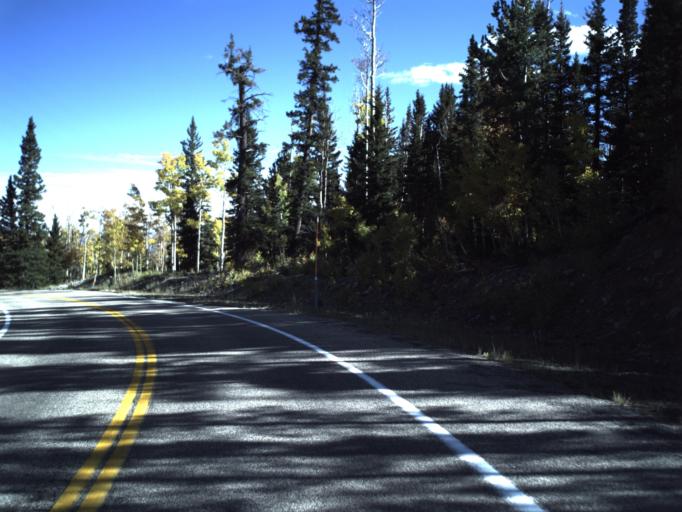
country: US
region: Utah
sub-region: Iron County
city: Parowan
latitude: 37.6554
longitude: -112.7148
